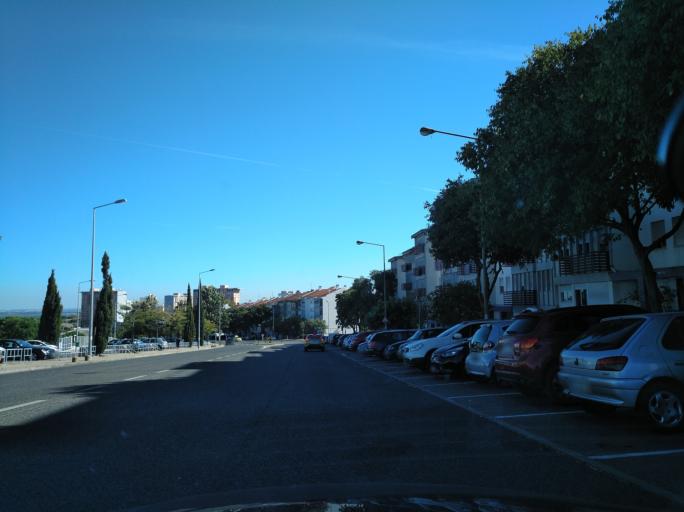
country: PT
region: Lisbon
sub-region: Loures
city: Moscavide
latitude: 38.7539
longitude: -9.1235
